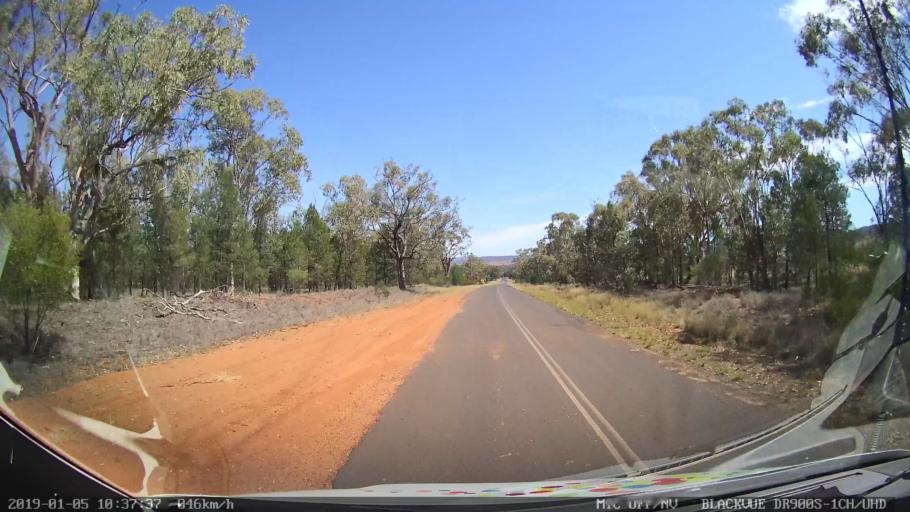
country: AU
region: New South Wales
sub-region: Gilgandra
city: Gilgandra
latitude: -31.4734
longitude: 148.9211
